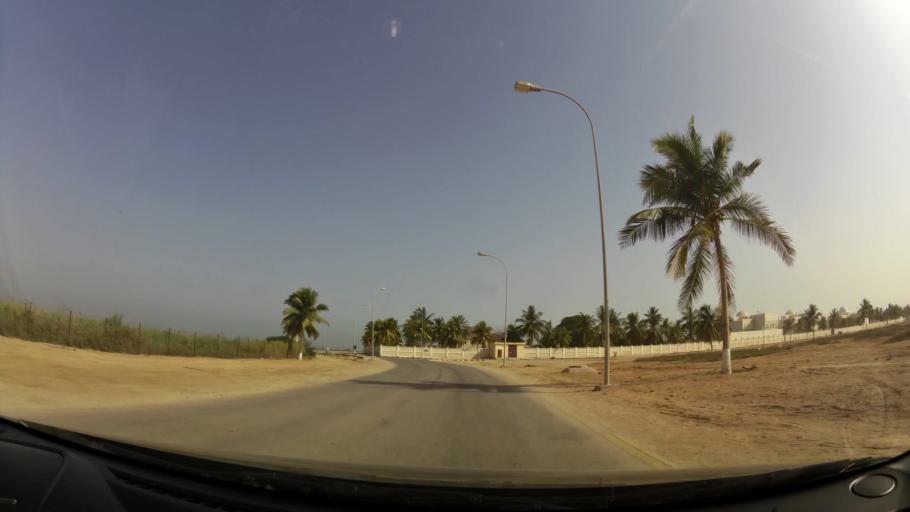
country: OM
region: Zufar
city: Salalah
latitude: 16.9973
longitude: 54.0651
